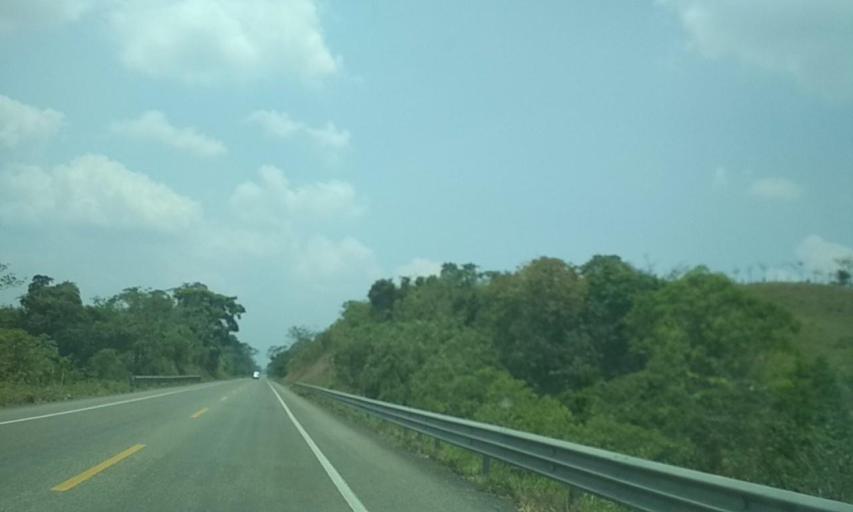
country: MX
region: Tabasco
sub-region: Huimanguillo
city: Francisco Rueda
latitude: 17.6625
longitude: -93.8567
